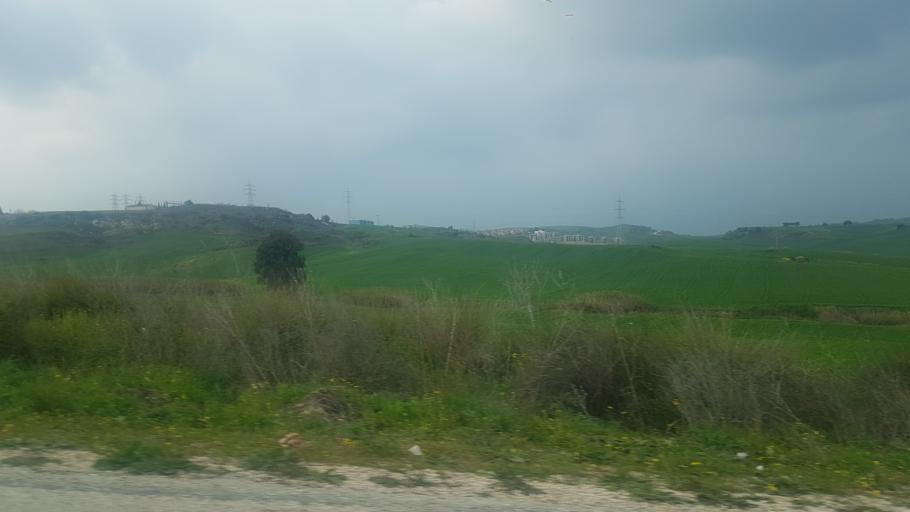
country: TR
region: Adana
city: Seyhan
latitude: 37.0476
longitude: 35.1975
